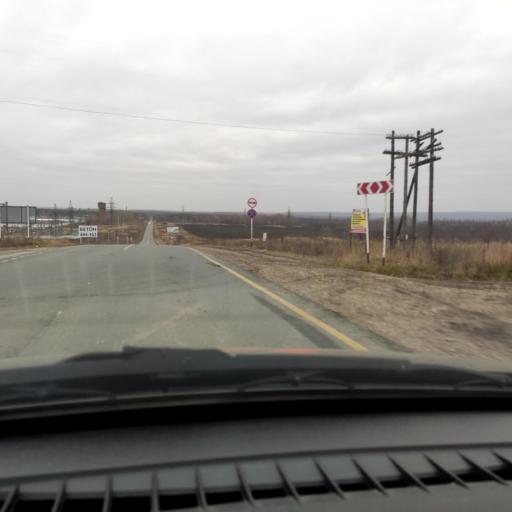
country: RU
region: Samara
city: Zhigulevsk
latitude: 53.3399
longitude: 49.4849
